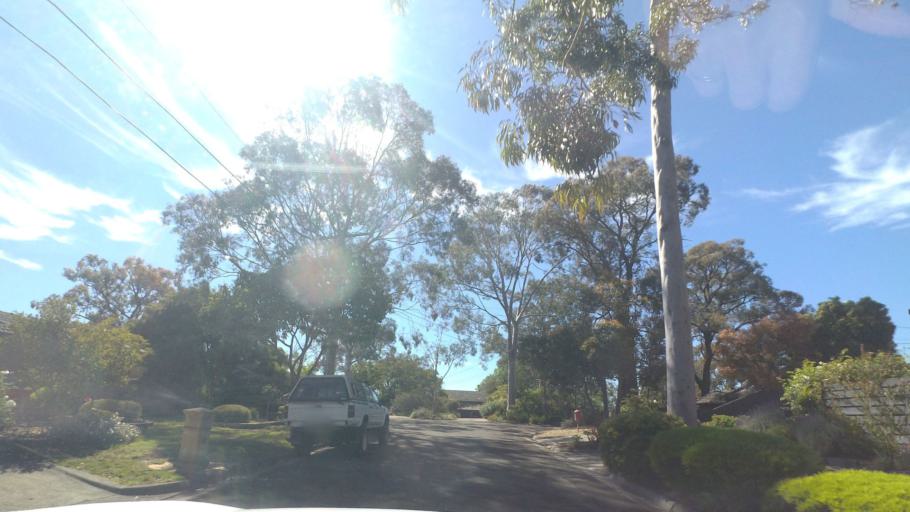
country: AU
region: Victoria
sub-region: Maroondah
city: Ringwood East
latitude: -37.8179
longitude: 145.2576
